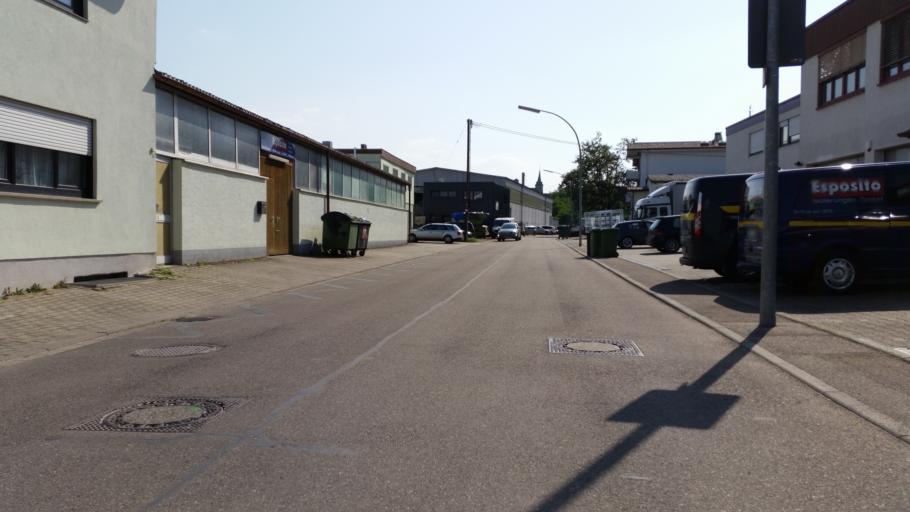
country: DE
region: Baden-Wuerttemberg
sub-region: Regierungsbezirk Stuttgart
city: Pleidelsheim
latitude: 48.9642
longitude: 9.1920
